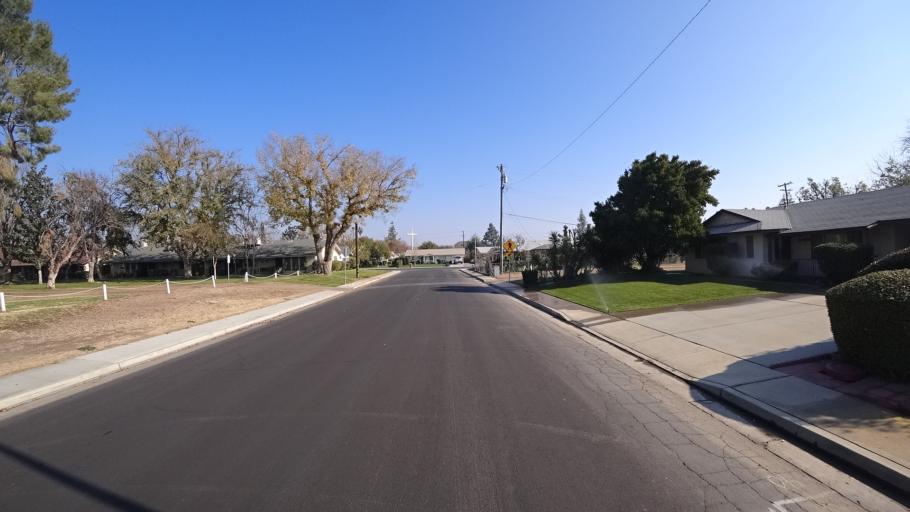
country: US
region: California
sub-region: Kern County
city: Bakersfield
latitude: 35.3456
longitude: -119.0631
